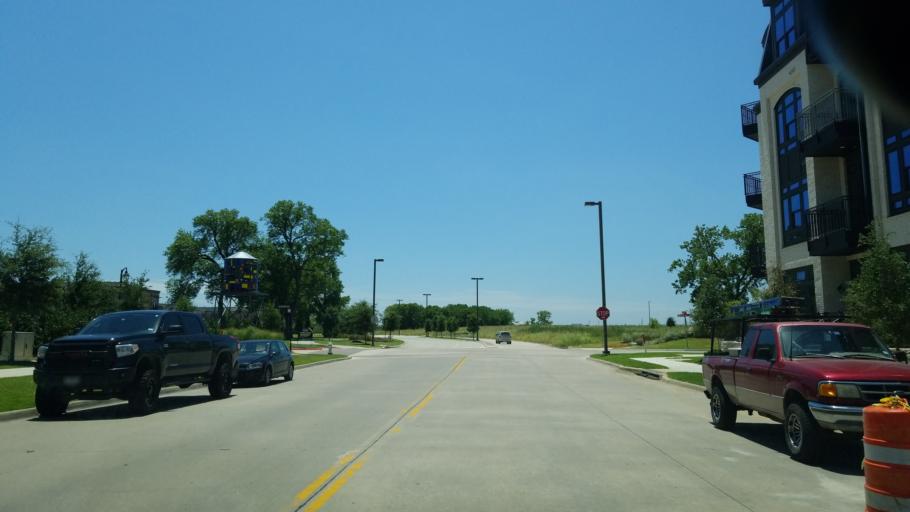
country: US
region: Texas
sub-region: Dallas County
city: Farmers Branch
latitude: 32.9178
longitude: -96.9105
